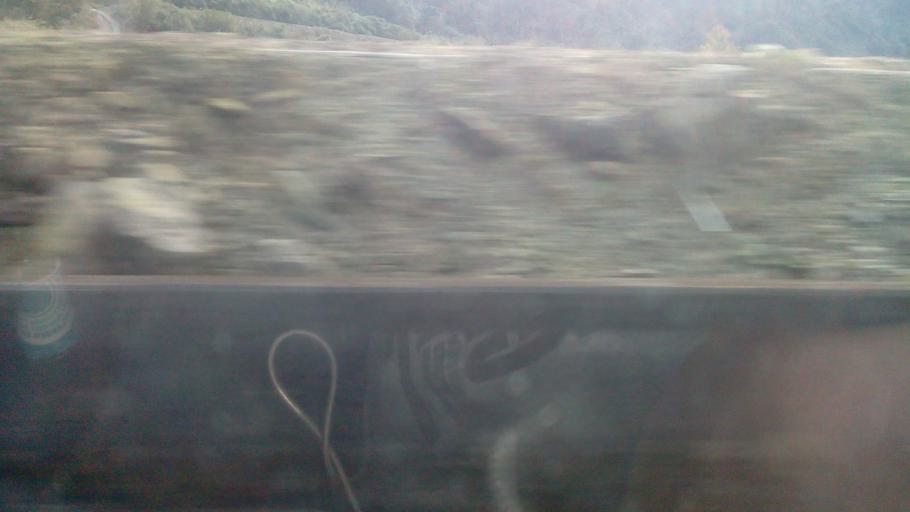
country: TW
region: Taiwan
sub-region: Yilan
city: Yilan
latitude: 24.5539
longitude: 121.4718
